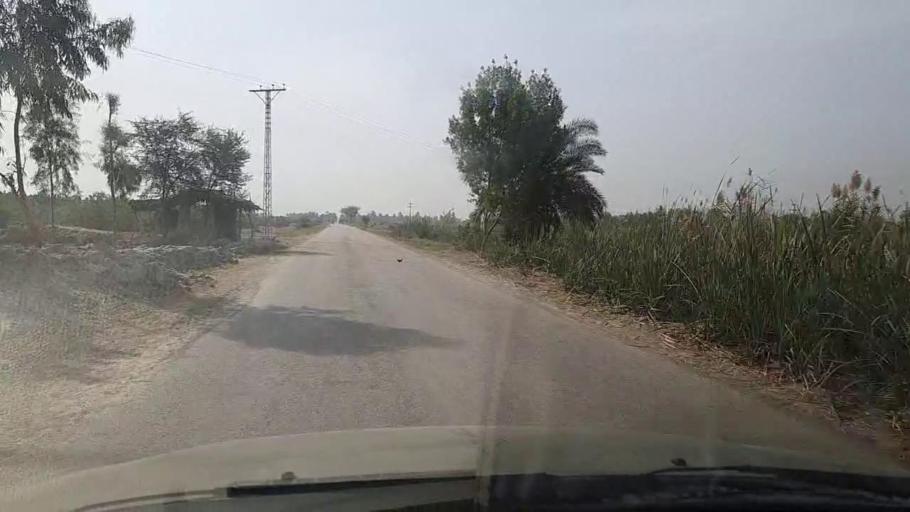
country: PK
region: Sindh
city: Gambat
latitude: 27.4757
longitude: 68.4718
